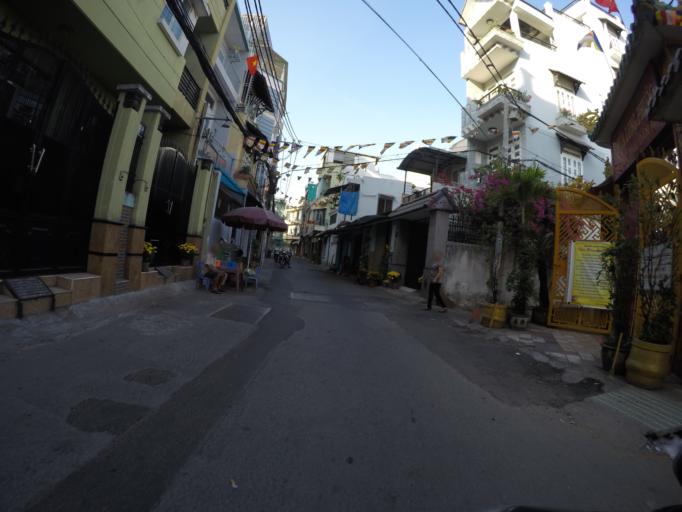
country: VN
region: Ho Chi Minh City
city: Quan Phu Nhuan
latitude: 10.7987
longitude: 106.6845
